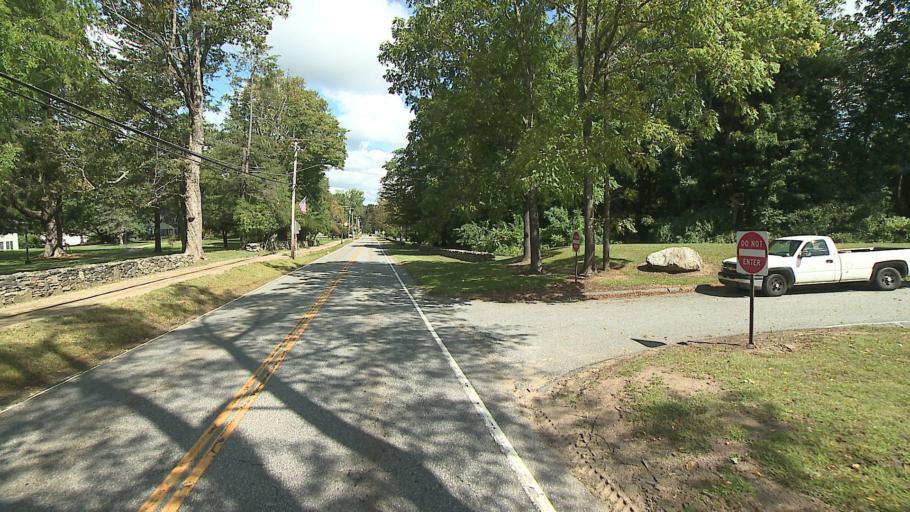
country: US
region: Connecticut
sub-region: Windham County
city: South Woodstock
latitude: 41.8941
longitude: -71.9621
